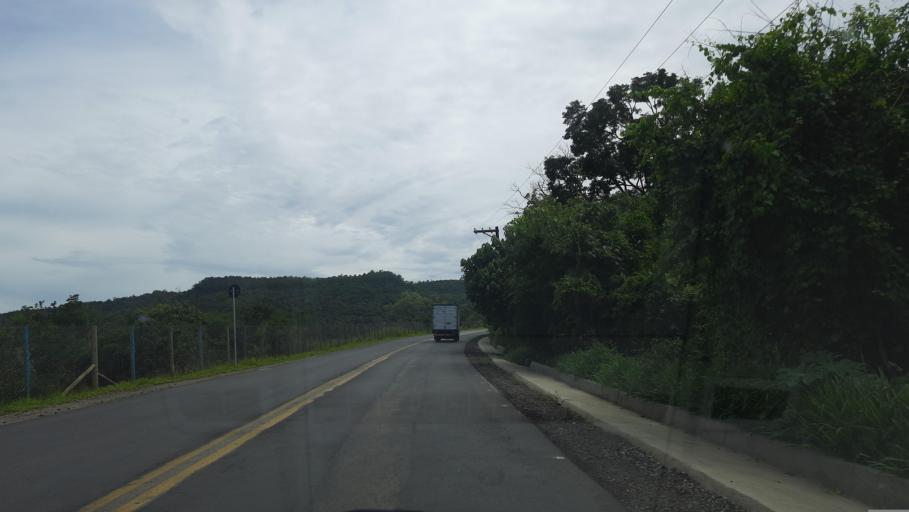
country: BR
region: Sao Paulo
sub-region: Franco Da Rocha
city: Franco da Rocha
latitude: -23.3417
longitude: -46.6616
